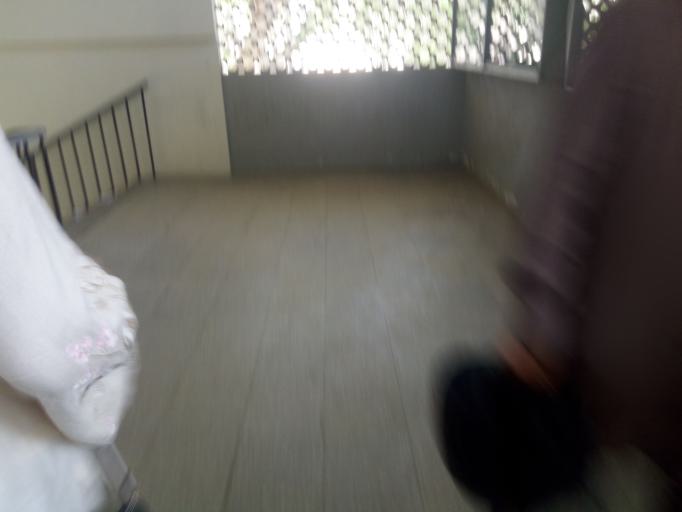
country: PK
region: Sindh
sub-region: Karachi District
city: Karachi
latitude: 24.9330
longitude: 67.1117
